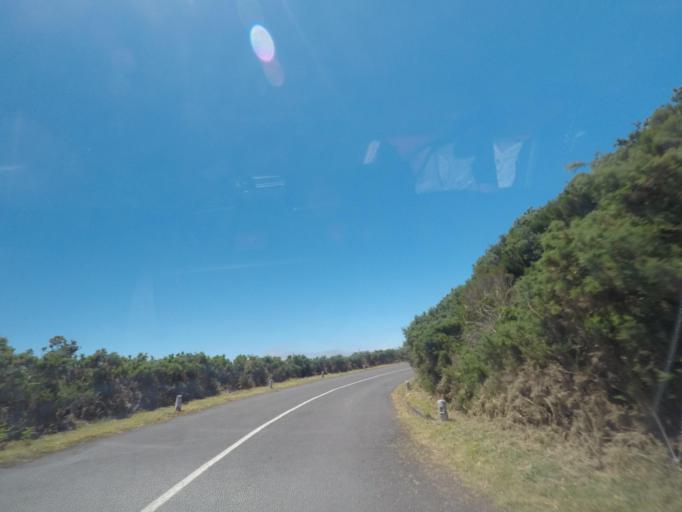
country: PT
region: Madeira
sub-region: Calheta
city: Faja da Ovelha
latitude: 32.8015
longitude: -17.1911
